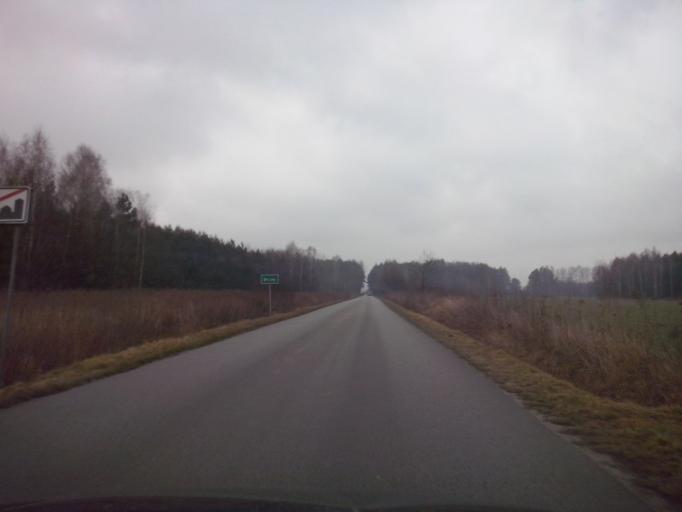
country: PL
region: Subcarpathian Voivodeship
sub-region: Powiat nizanski
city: Bieliny
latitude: 50.4520
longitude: 22.2858
